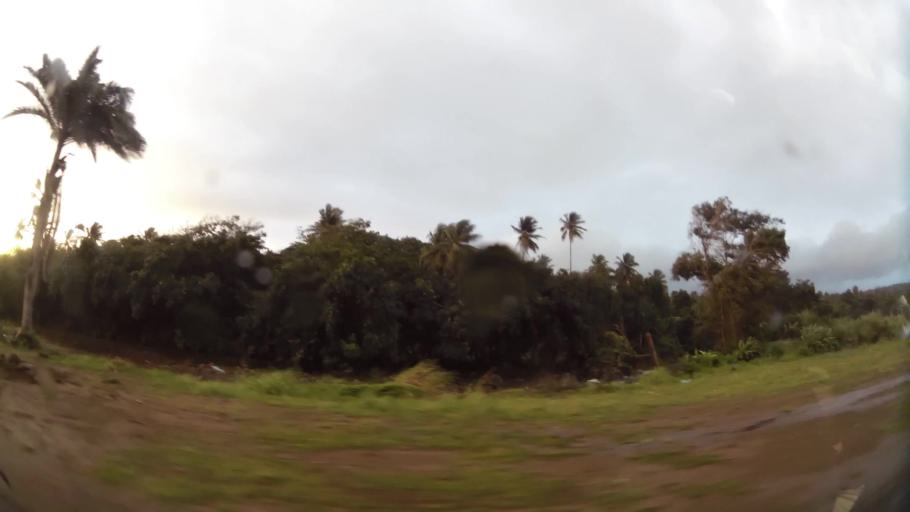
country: DM
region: Saint Andrew
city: Marigot
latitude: 15.5472
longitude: -61.2962
